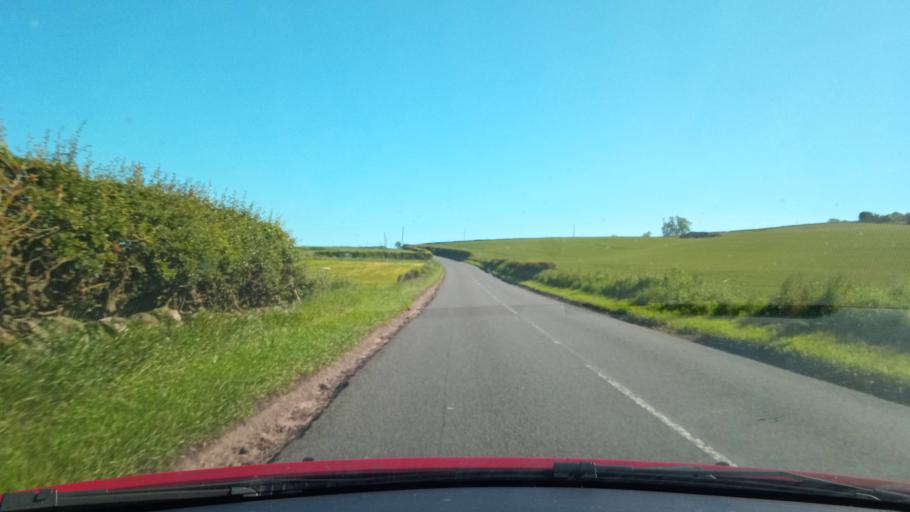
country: GB
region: Scotland
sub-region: The Scottish Borders
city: Duns
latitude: 55.7919
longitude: -2.3377
